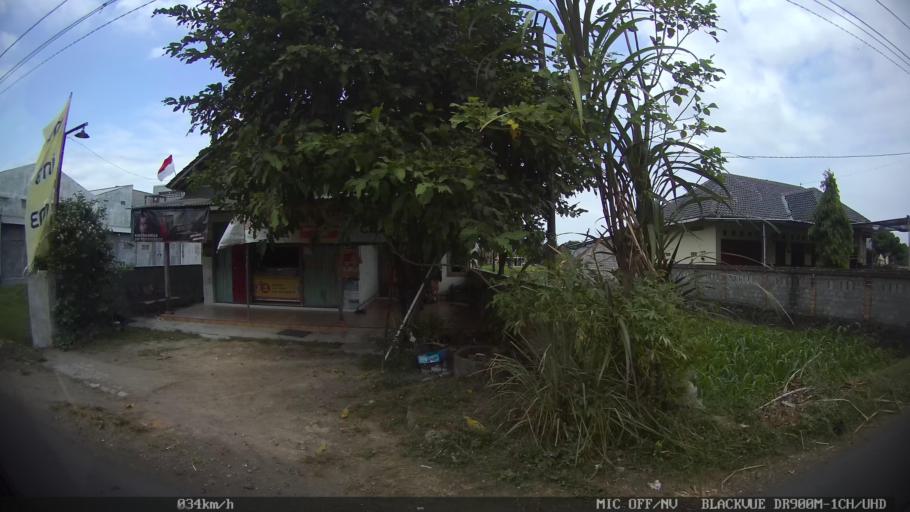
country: ID
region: Daerah Istimewa Yogyakarta
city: Depok
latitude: -7.8134
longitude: 110.4703
